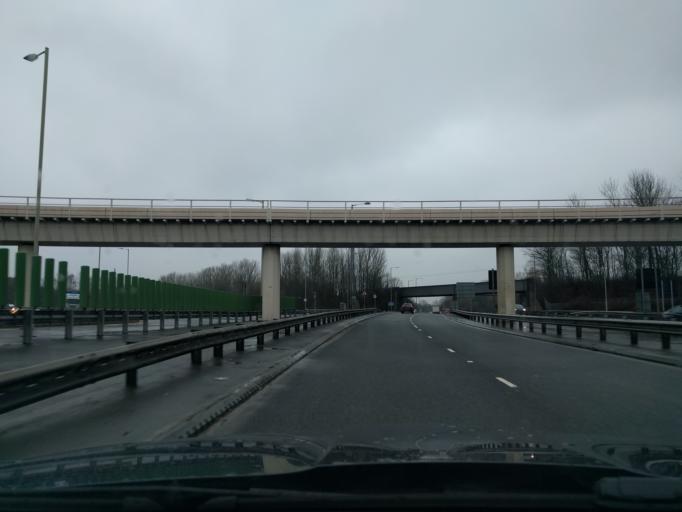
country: GB
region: England
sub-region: South Tyneside
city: Jarrow
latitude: 54.9778
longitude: -1.4807
